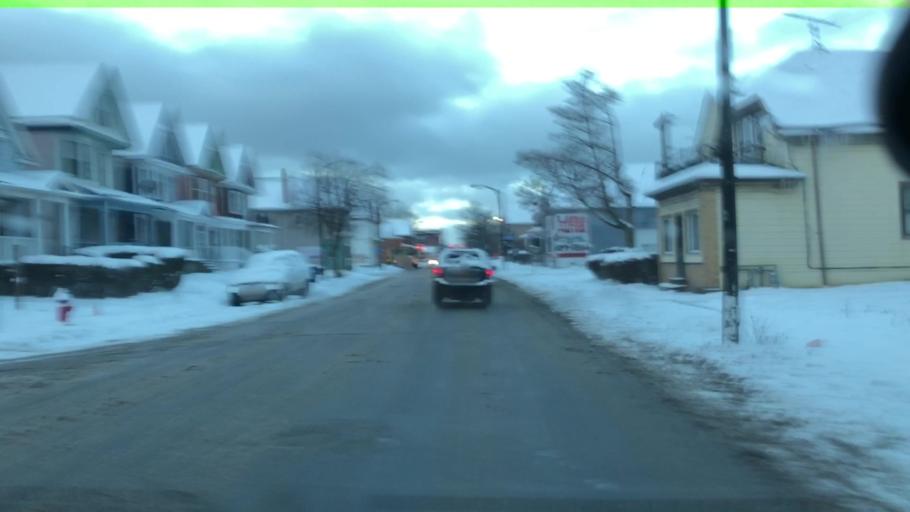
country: US
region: New York
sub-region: Erie County
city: Sloan
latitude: 42.9035
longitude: -78.8326
